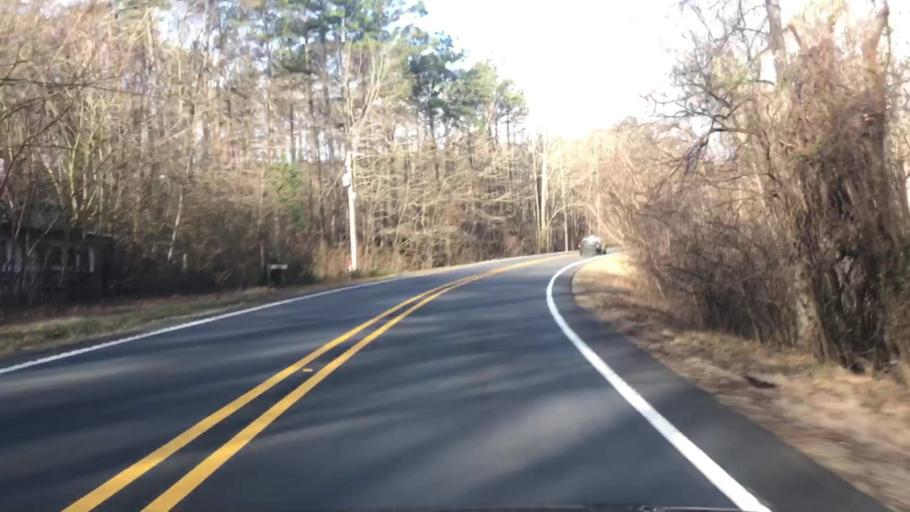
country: US
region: Arkansas
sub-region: Montgomery County
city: Mount Ida
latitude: 34.5229
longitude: -93.3989
